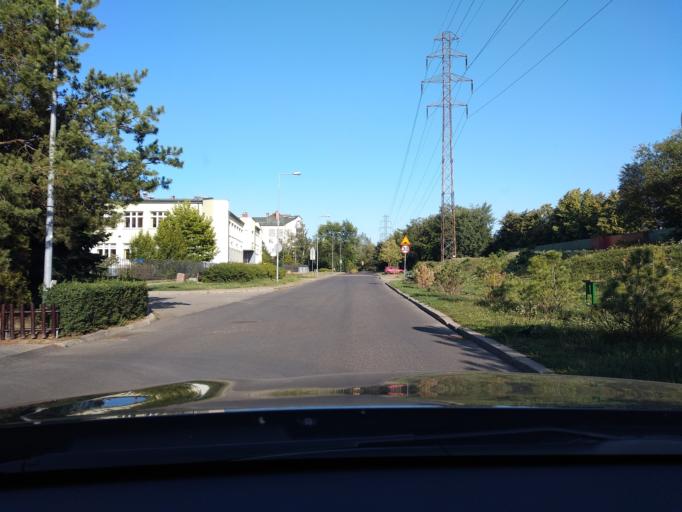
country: PL
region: Masovian Voivodeship
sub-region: Warszawa
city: Ursynow
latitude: 52.1278
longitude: 21.0567
